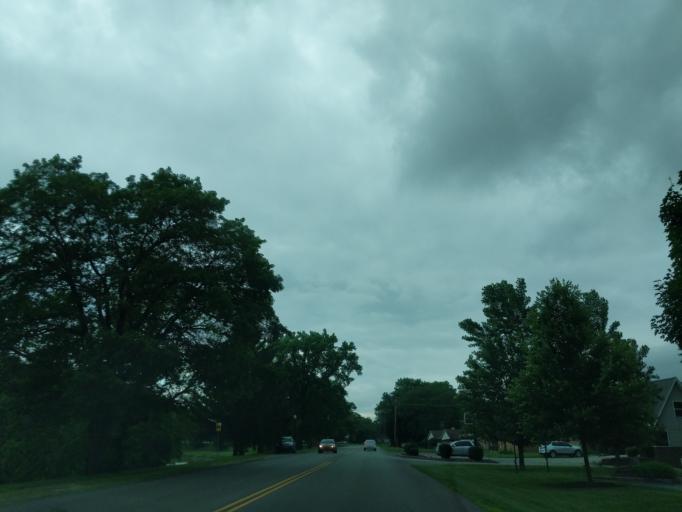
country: US
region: Indiana
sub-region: Delaware County
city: Muncie
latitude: 40.1951
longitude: -85.3940
